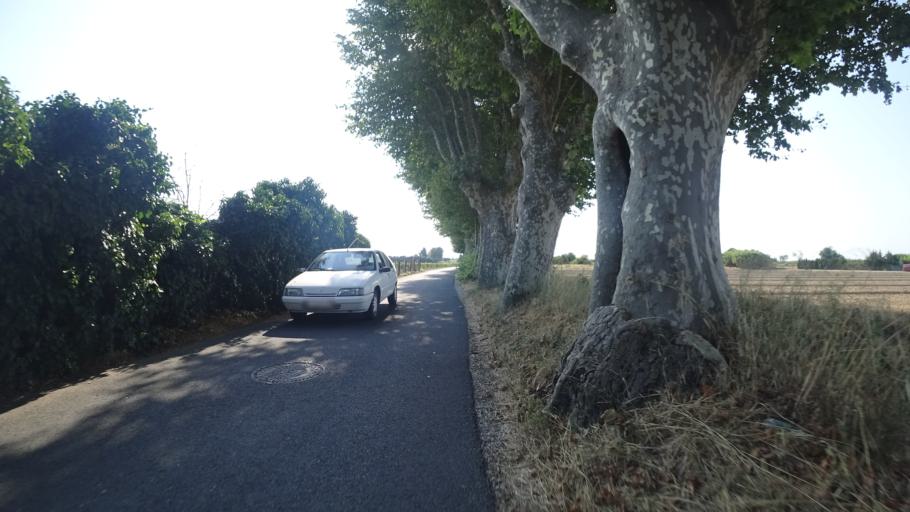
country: FR
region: Languedoc-Roussillon
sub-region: Departement des Pyrenees-Orientales
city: Claira
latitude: 42.7593
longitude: 2.9653
